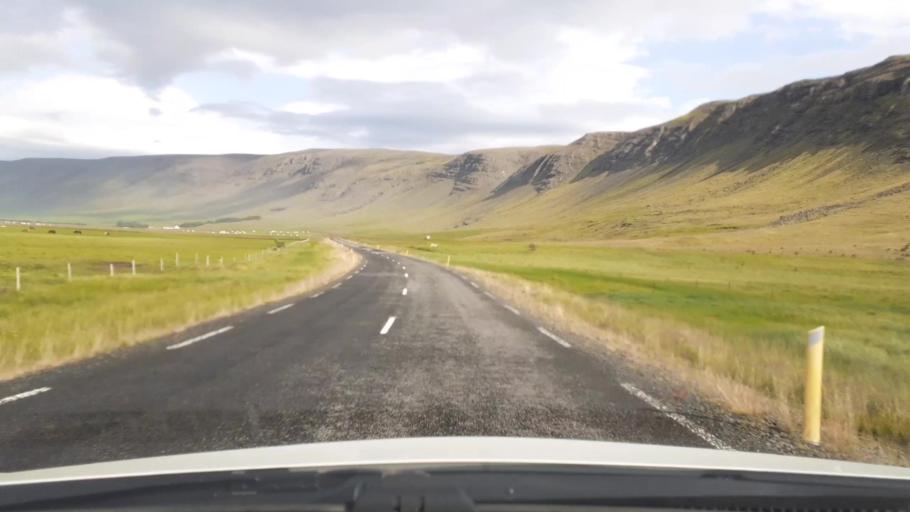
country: IS
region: Capital Region
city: Mosfellsbaer
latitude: 64.3226
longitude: -21.5003
